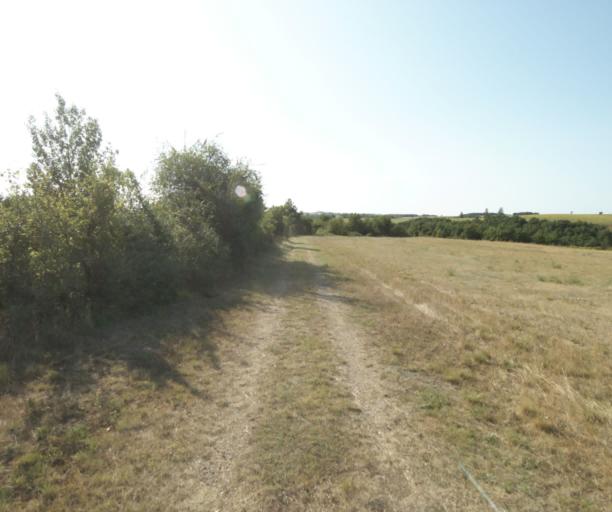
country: FR
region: Midi-Pyrenees
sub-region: Departement de la Haute-Garonne
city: Saint-Felix-Lauragais
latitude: 43.4440
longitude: 1.8219
